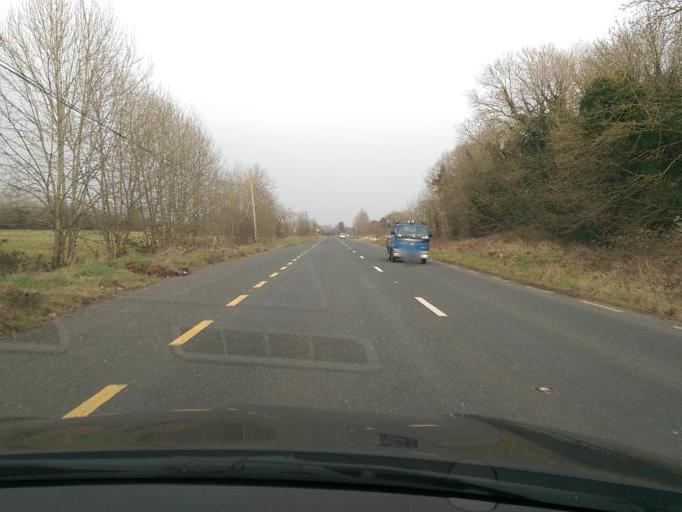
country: IE
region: Connaught
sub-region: Roscommon
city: Roscommon
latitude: 53.6546
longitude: -8.1027
